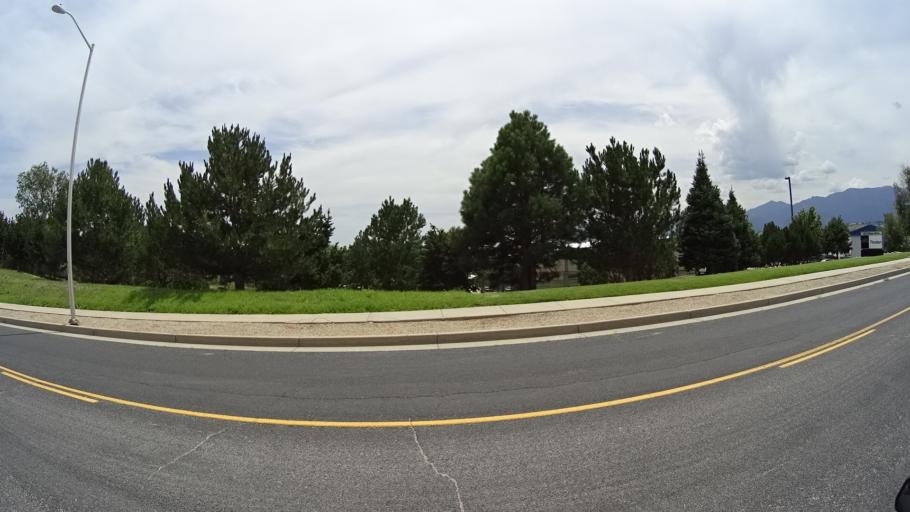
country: US
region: Colorado
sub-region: El Paso County
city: Colorado Springs
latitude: 38.9010
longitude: -104.8316
